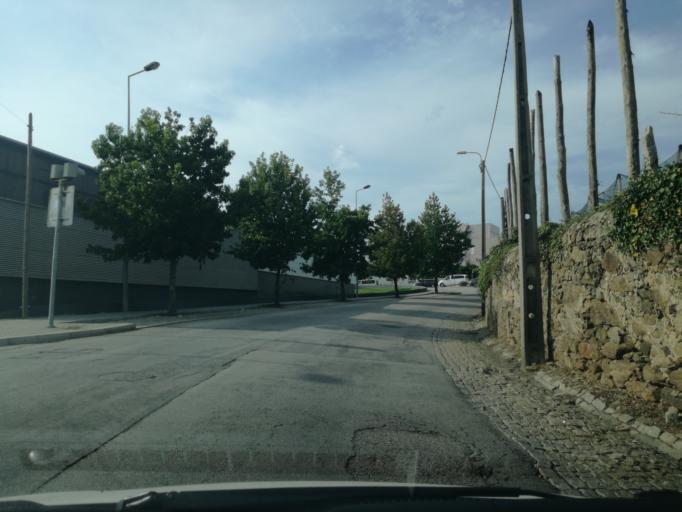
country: PT
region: Porto
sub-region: Vila Nova de Gaia
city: Azenha
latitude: 41.0615
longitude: -8.6282
